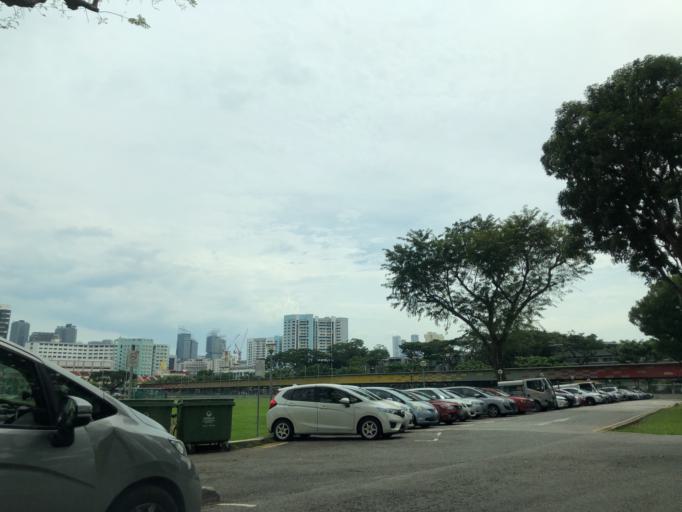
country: SG
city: Singapore
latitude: 1.3112
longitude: 103.8488
